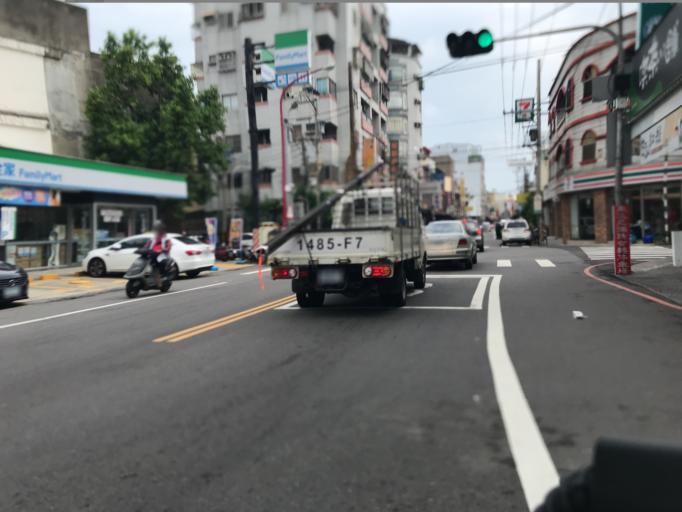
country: TW
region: Taiwan
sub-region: Miaoli
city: Miaoli
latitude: 24.6917
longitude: 120.8664
